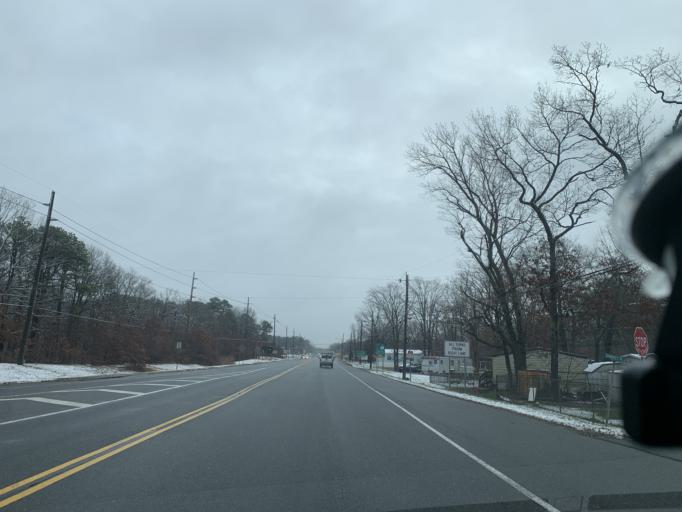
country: US
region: New Jersey
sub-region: Atlantic County
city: Pomona
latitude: 39.4327
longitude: -74.5828
